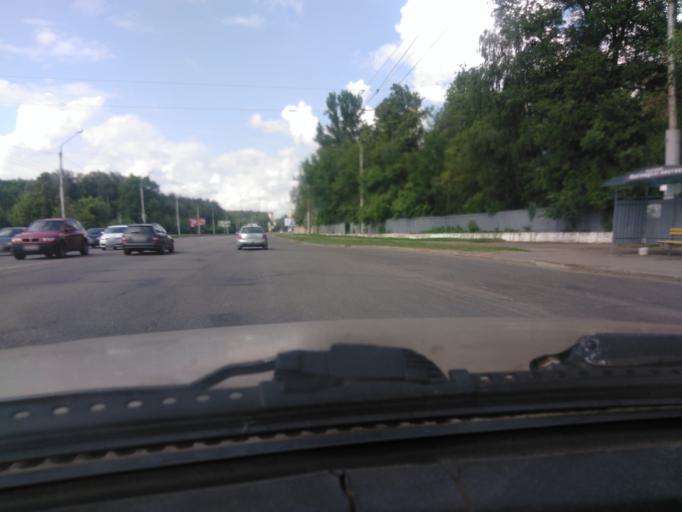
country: BY
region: Mogilev
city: Mahilyow
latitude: 53.9424
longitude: 30.3548
